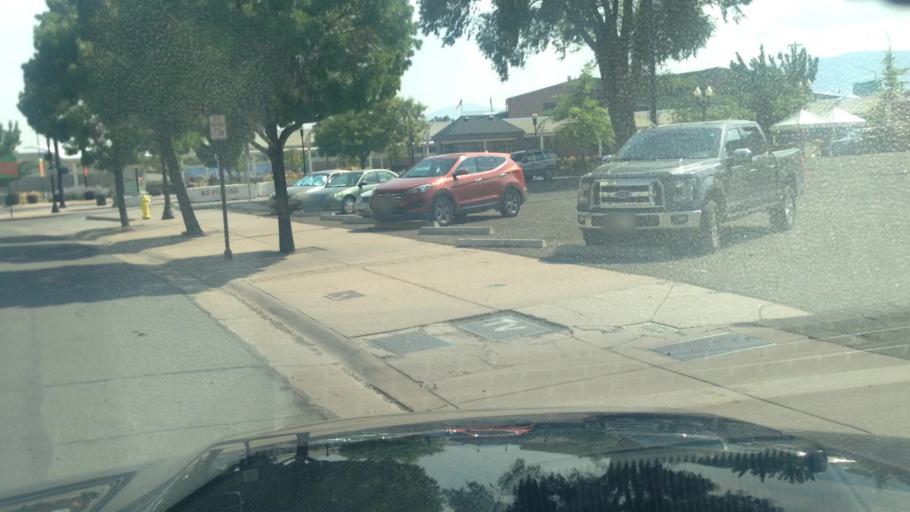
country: US
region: Nevada
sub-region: Washoe County
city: Sparks
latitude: 39.5355
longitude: -119.7607
